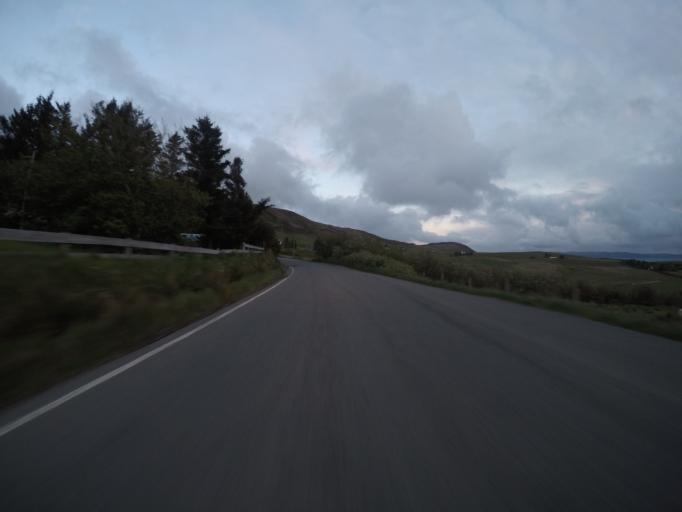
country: GB
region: Scotland
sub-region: Highland
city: Portree
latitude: 57.6171
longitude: -6.3719
